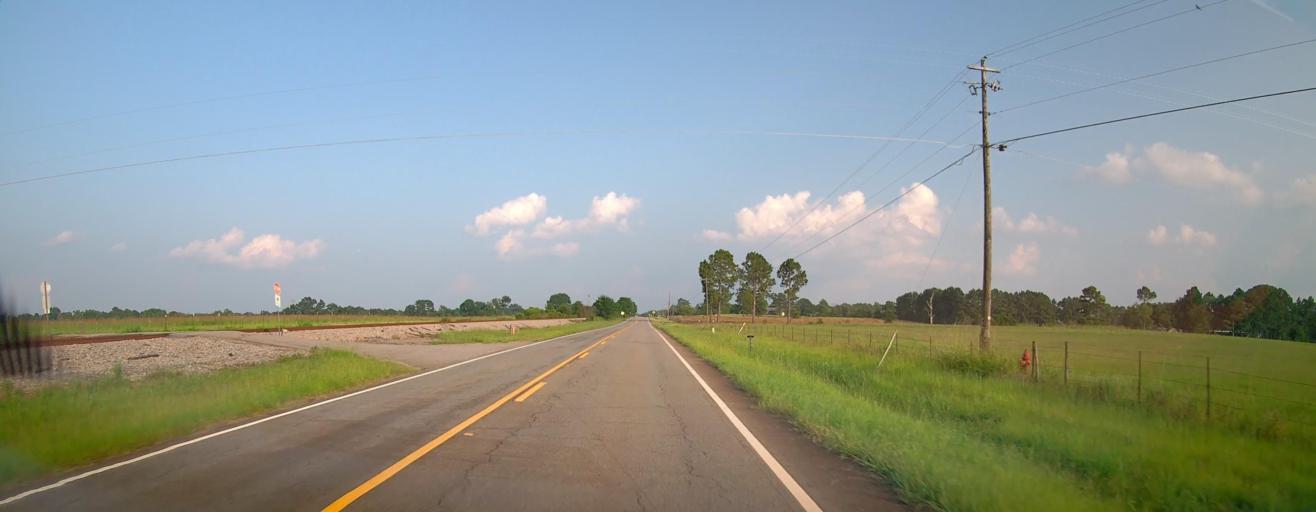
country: US
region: Georgia
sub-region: Jones County
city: Gray
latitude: 33.0391
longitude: -83.5459
